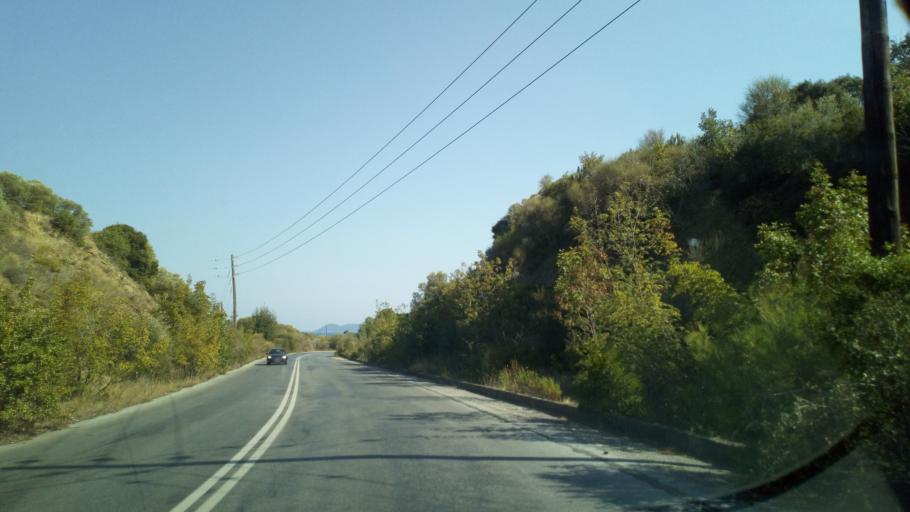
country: GR
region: Central Macedonia
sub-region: Nomos Thessalonikis
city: Stavros
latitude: 40.6162
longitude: 23.7756
